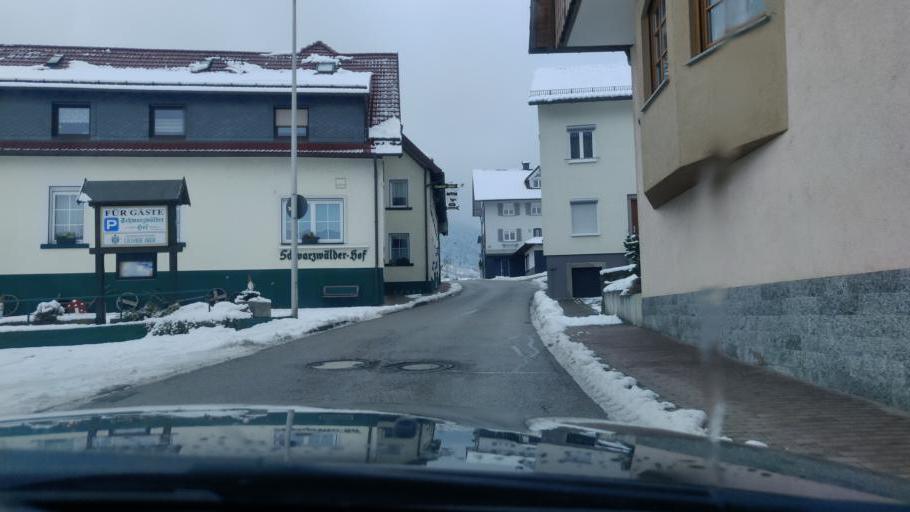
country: DE
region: Baden-Wuerttemberg
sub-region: Freiburg Region
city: Kappelrodeck
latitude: 48.5852
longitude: 8.1028
